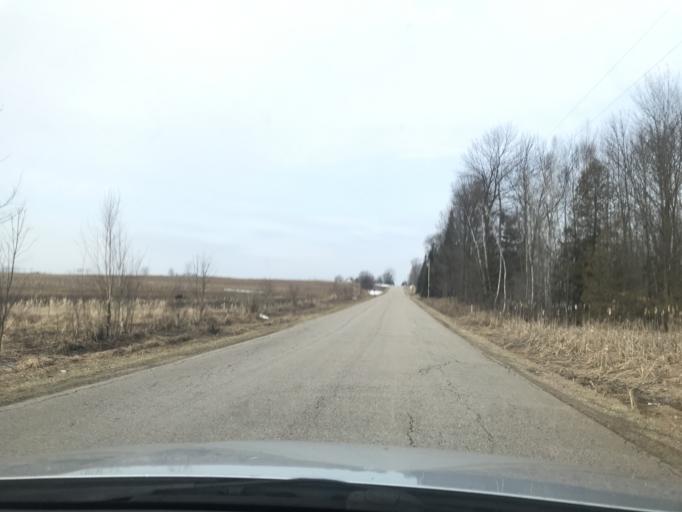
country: US
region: Wisconsin
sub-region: Oconto County
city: Oconto Falls
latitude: 44.8505
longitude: -88.1536
